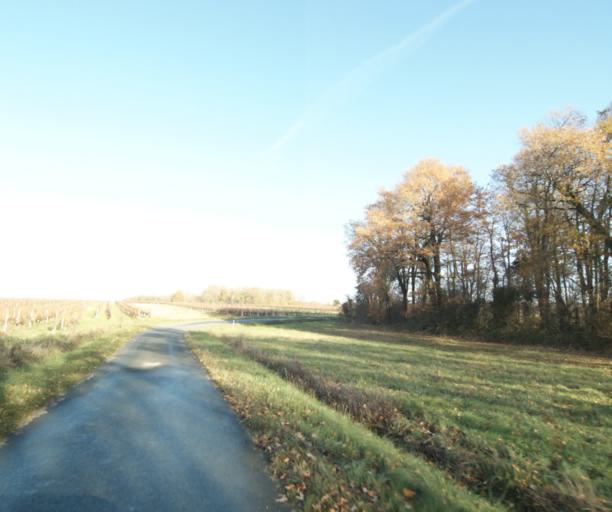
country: FR
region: Poitou-Charentes
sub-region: Departement de la Charente-Maritime
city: Burie
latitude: 45.7768
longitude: -0.4465
